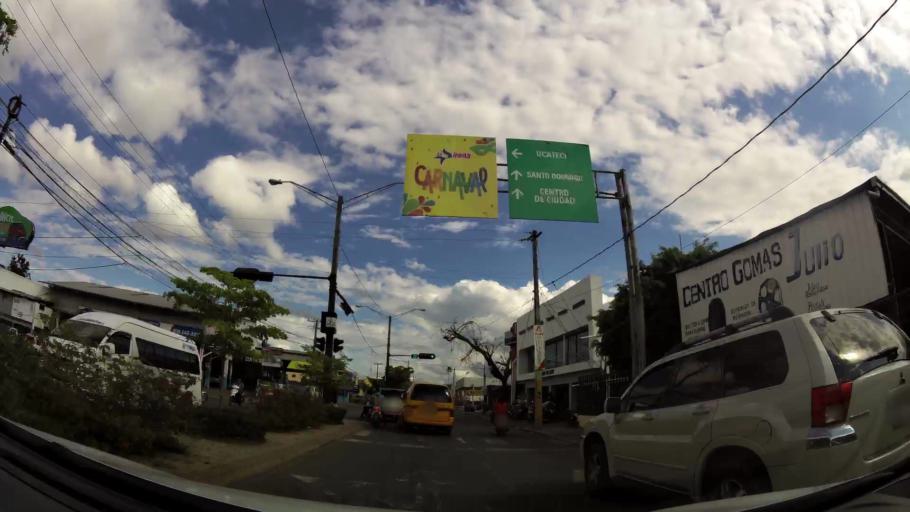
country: DO
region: La Vega
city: Concepcion de La Vega
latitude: 19.2265
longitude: -70.5235
